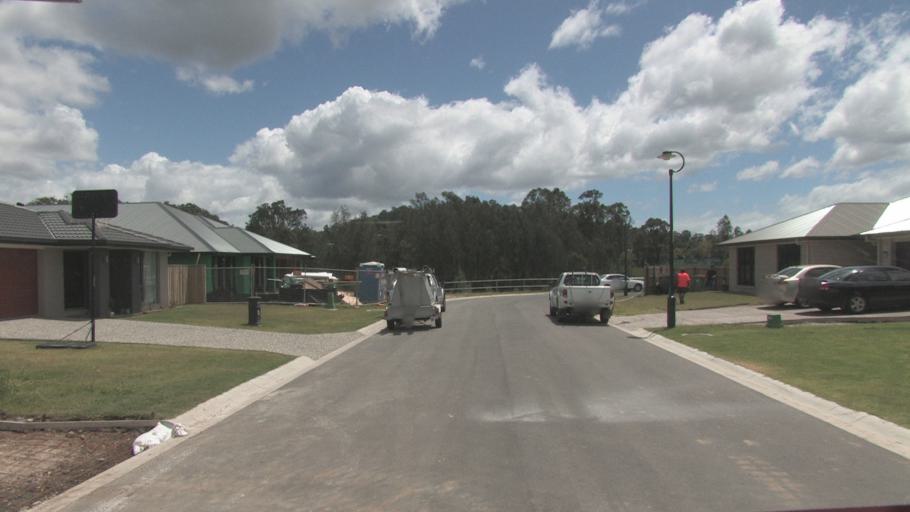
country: AU
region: Queensland
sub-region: Logan
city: Waterford West
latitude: -27.6830
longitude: 153.1709
